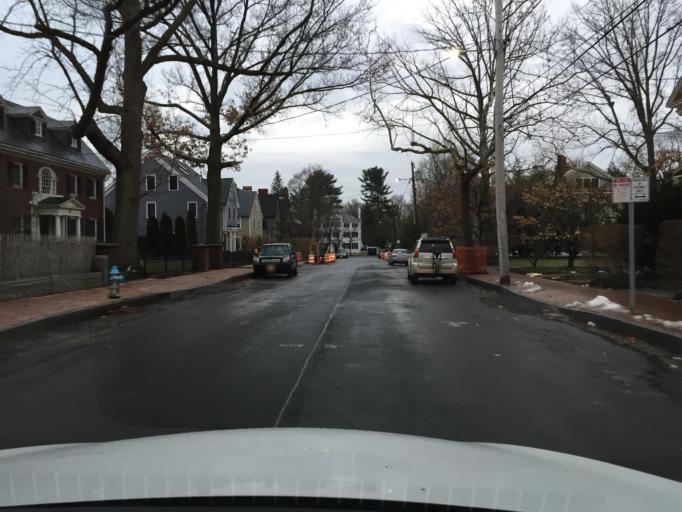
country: US
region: Massachusetts
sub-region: Middlesex County
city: Cambridge
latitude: 42.3779
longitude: -71.1390
